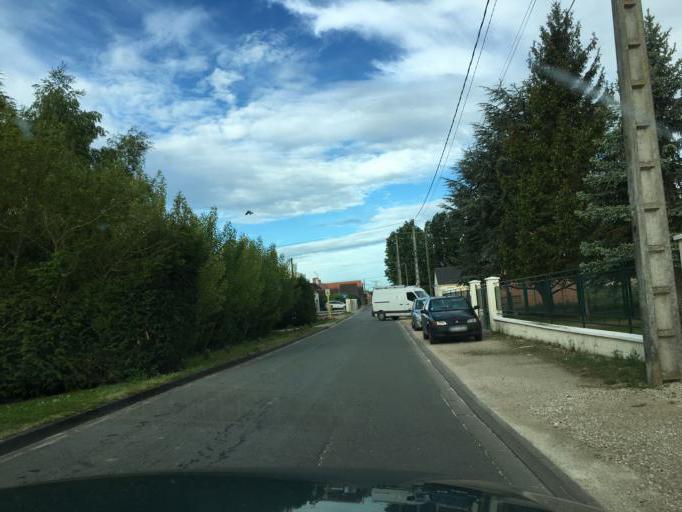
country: FR
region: Centre
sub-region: Departement du Loiret
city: Ingre
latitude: 47.9021
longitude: 1.8066
